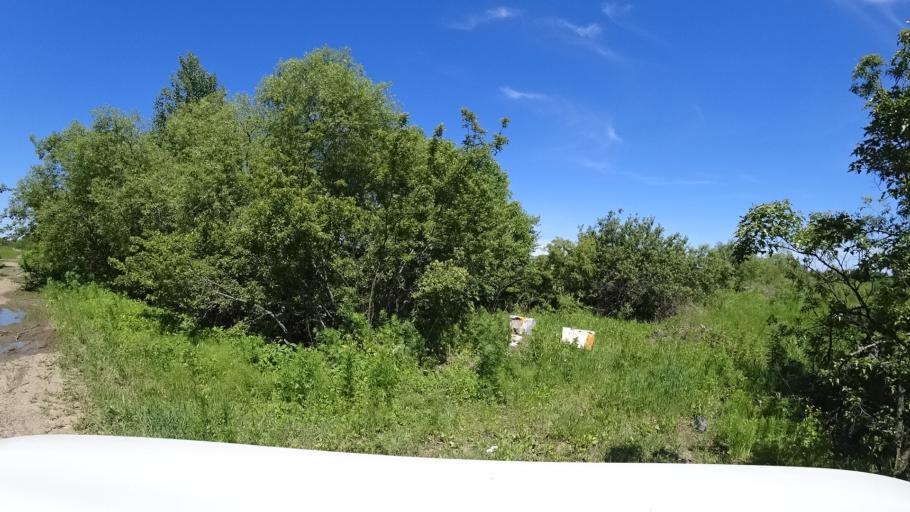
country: RU
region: Khabarovsk Krai
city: Topolevo
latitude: 48.4884
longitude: 135.1773
